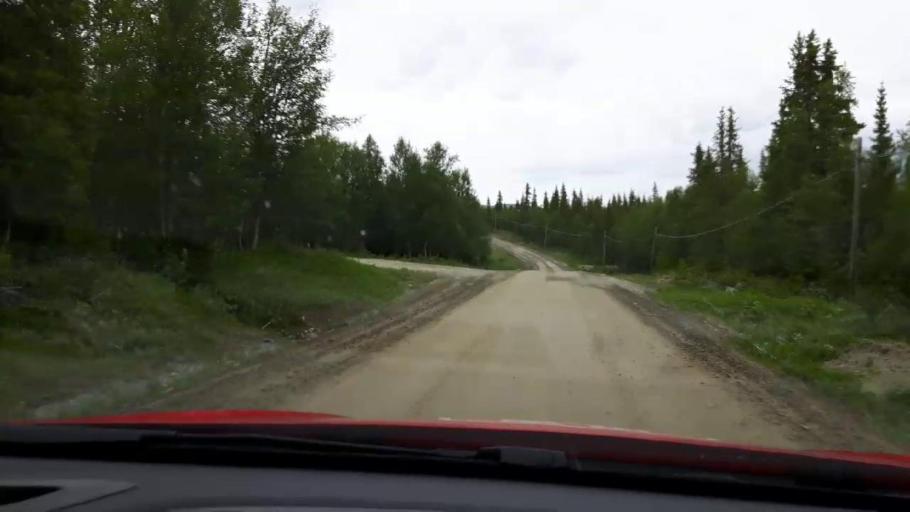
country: SE
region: Jaemtland
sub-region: Are Kommun
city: Are
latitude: 62.8325
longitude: 12.8056
